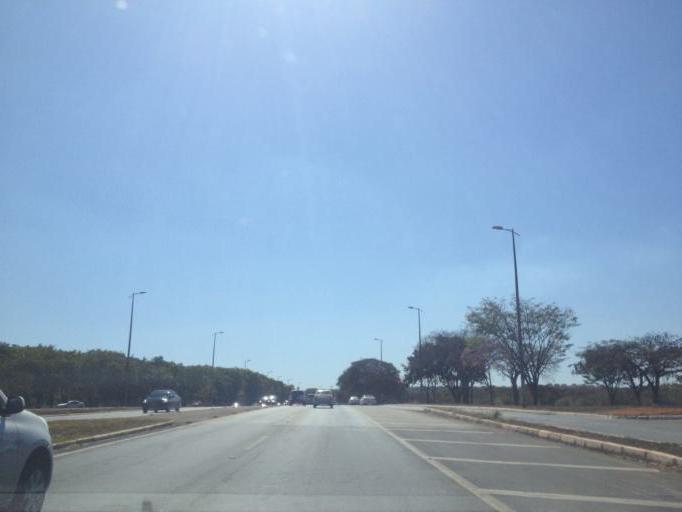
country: BR
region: Federal District
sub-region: Brasilia
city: Brasilia
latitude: -15.8441
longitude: -47.9314
